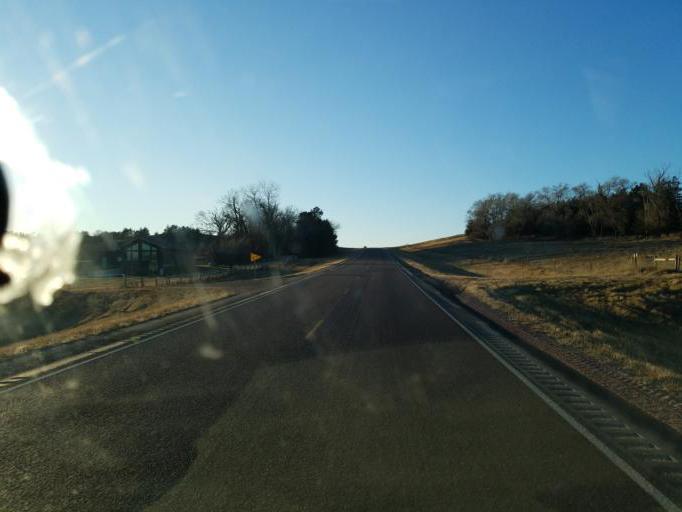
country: US
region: South Dakota
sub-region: Bon Homme County
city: Springfield
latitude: 42.8658
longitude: -97.9475
